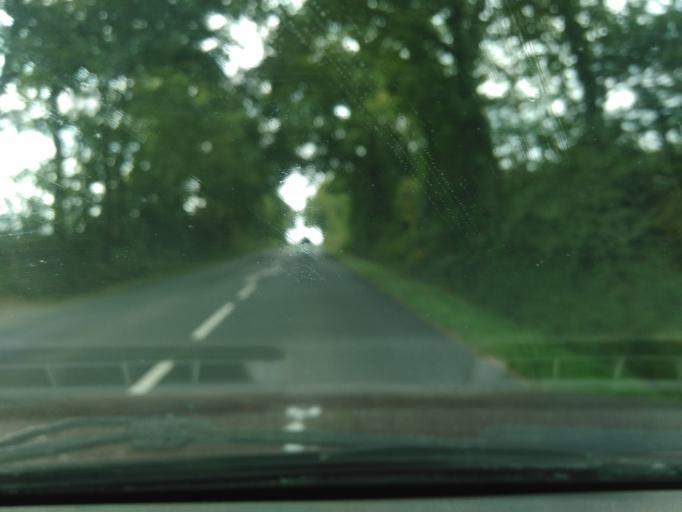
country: FR
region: Pays de la Loire
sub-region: Departement de la Vendee
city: Dompierre-sur-Yon
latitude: 46.7332
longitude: -1.3747
